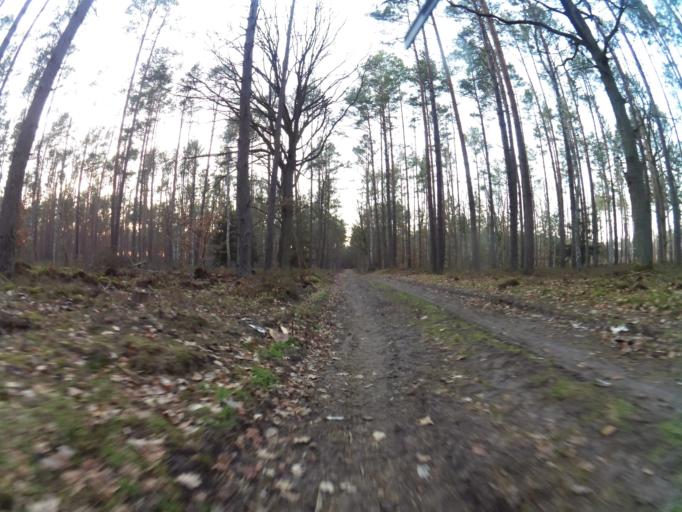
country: PL
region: West Pomeranian Voivodeship
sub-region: Powiat policki
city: Nowe Warpno
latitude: 53.6937
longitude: 14.3261
